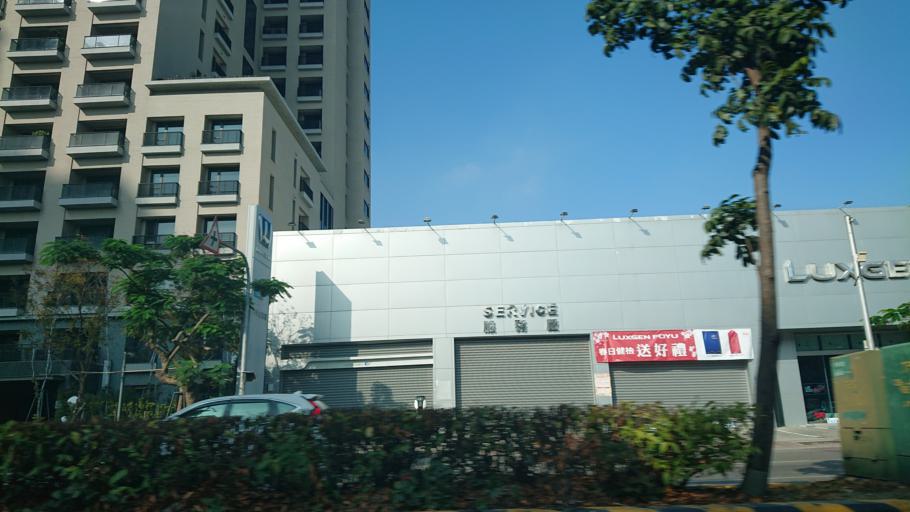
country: TW
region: Taiwan
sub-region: Tainan
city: Tainan
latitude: 23.0011
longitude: 120.1870
